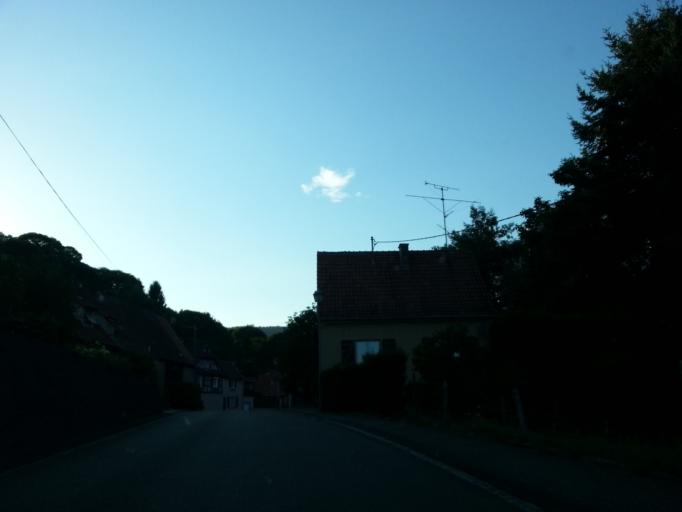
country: FR
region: Alsace
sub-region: Departement du Bas-Rhin
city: Soultz-sous-Forets
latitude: 48.9851
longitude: 7.8716
